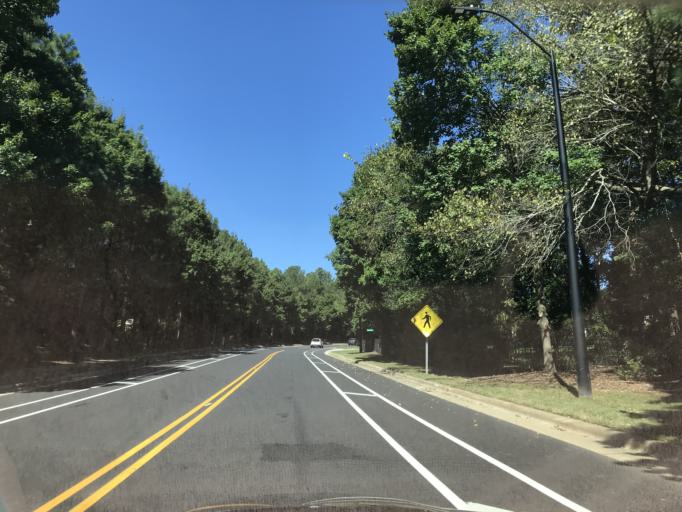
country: US
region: North Carolina
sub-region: Wake County
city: Wake Forest
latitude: 35.9491
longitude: -78.5635
